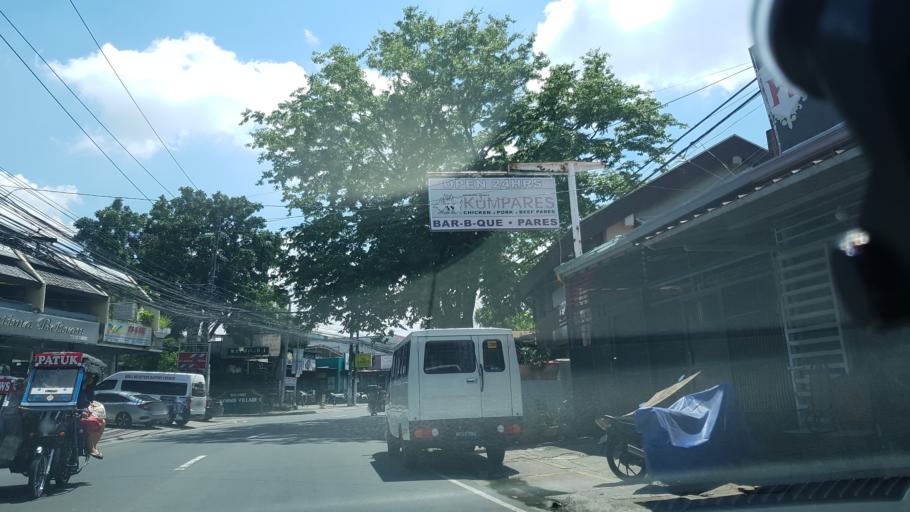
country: PH
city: Sambayanihan People's Village
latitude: 14.4557
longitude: 121.0311
